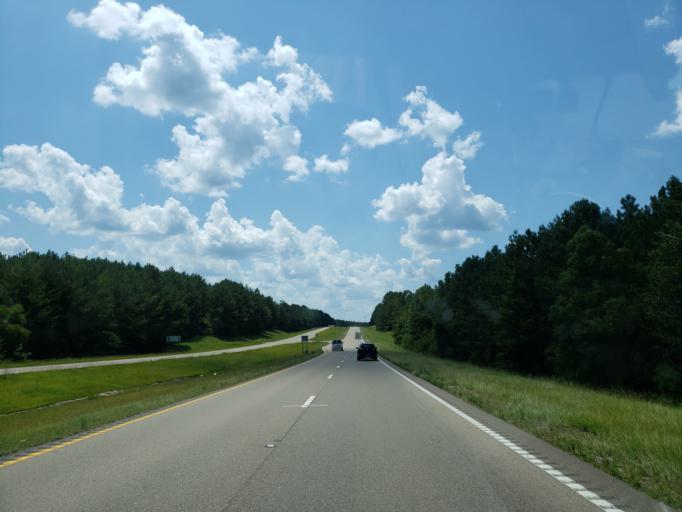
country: US
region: Mississippi
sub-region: Perry County
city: New Augusta
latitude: 31.1536
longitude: -88.9019
